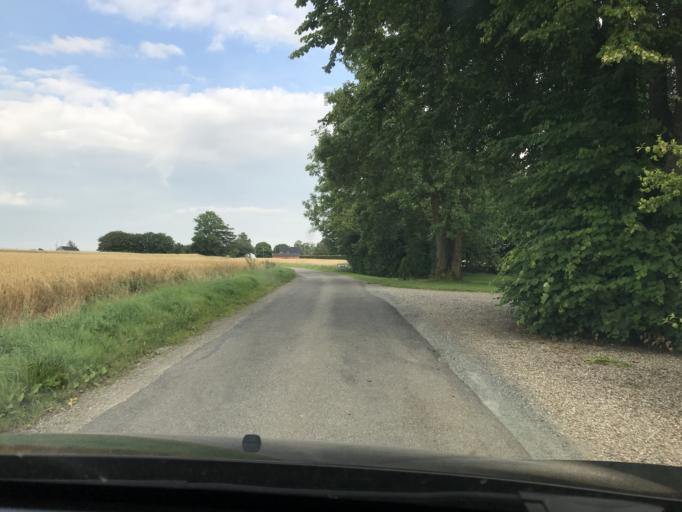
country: DK
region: South Denmark
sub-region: Vejle Kommune
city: Jelling
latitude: 55.8052
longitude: 9.4249
